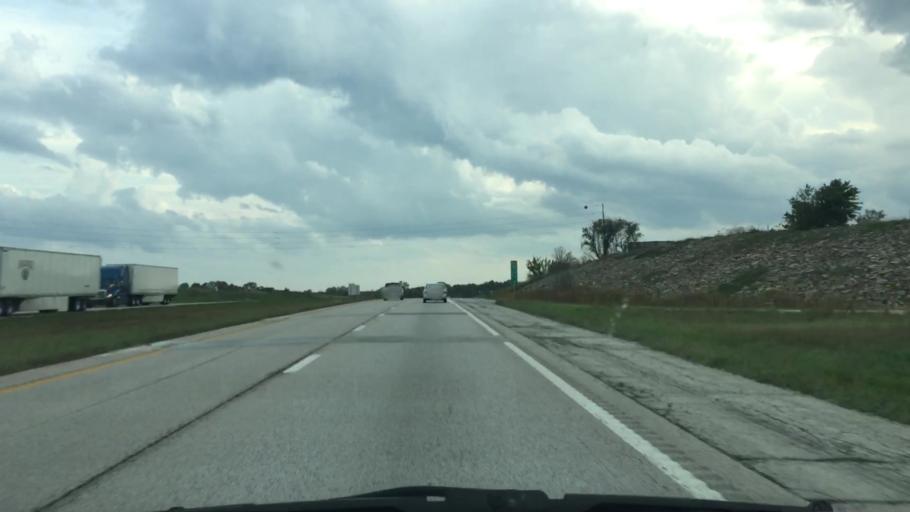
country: US
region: Missouri
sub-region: Clinton County
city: Cameron
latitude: 39.7304
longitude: -94.2208
